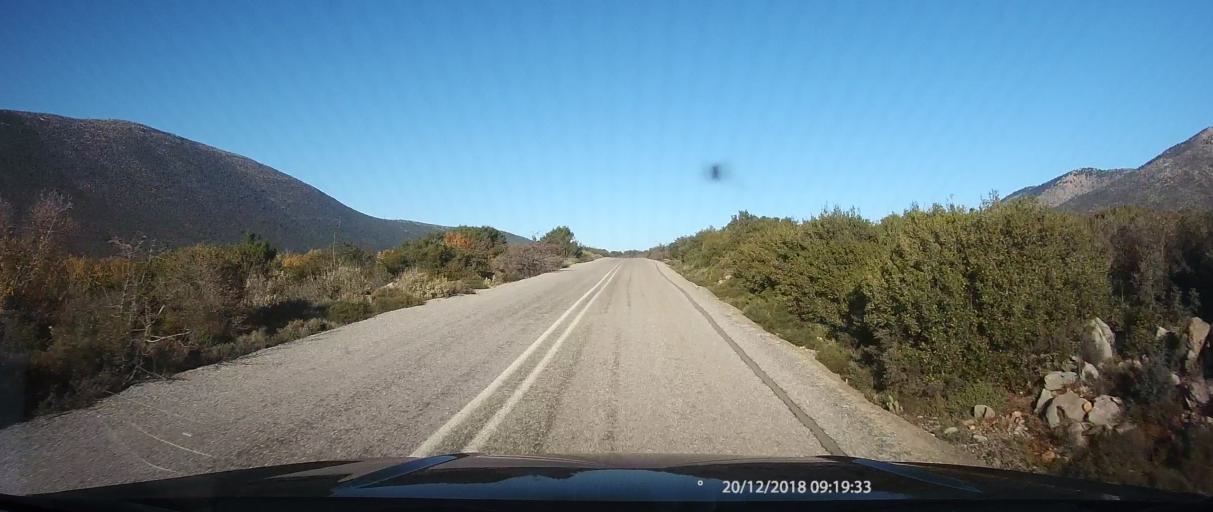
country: GR
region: Peloponnese
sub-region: Nomos Lakonias
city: Molaoi
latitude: 36.9198
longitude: 22.9379
